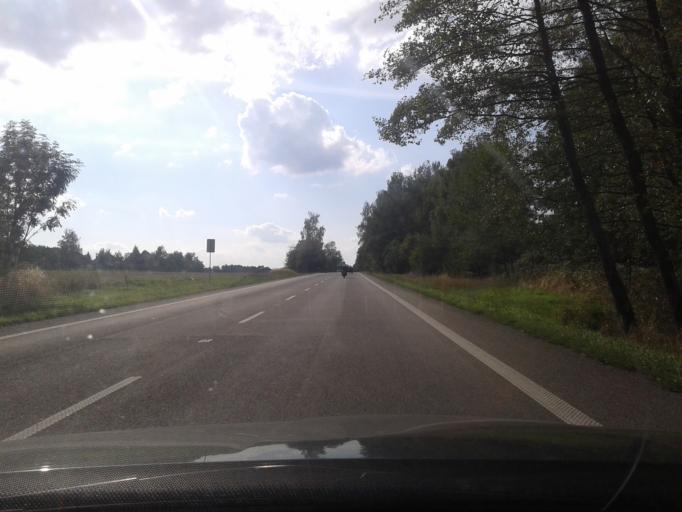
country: CZ
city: Dolni Lutyne
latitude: 49.9008
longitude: 18.4166
